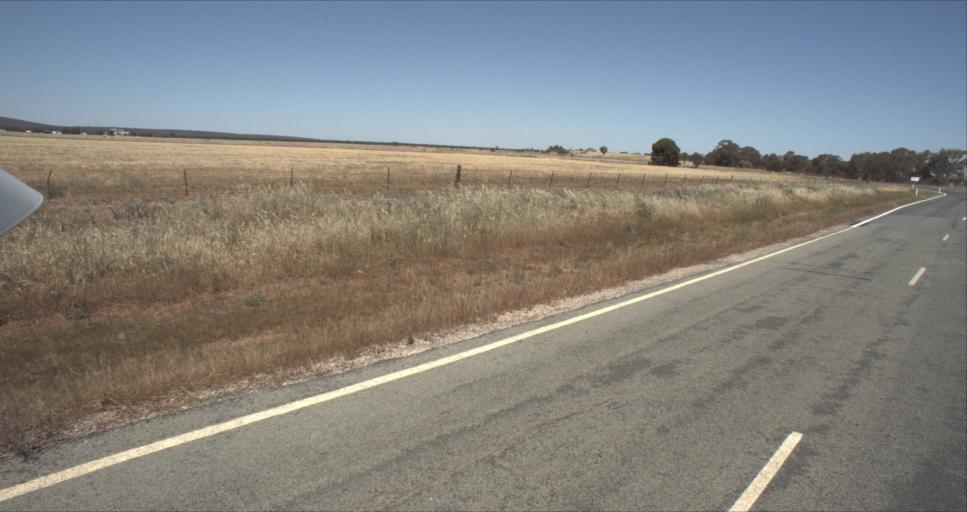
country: AU
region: New South Wales
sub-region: Leeton
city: Leeton
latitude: -34.4917
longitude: 146.4322
